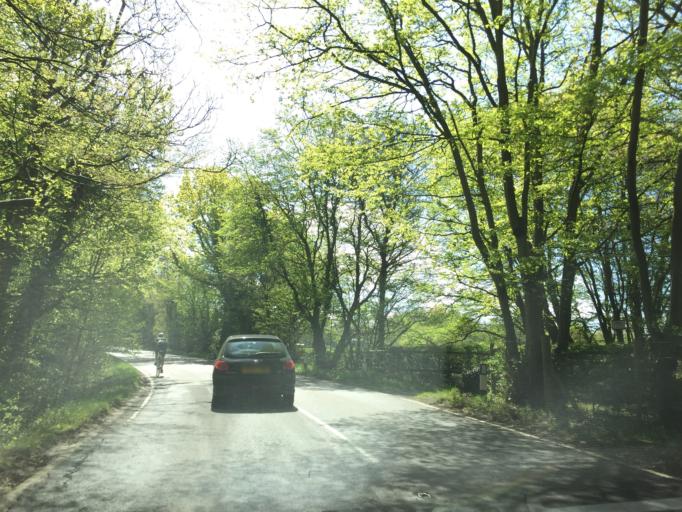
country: GB
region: England
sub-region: Kent
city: Edenbridge
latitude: 51.1335
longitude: 0.1070
